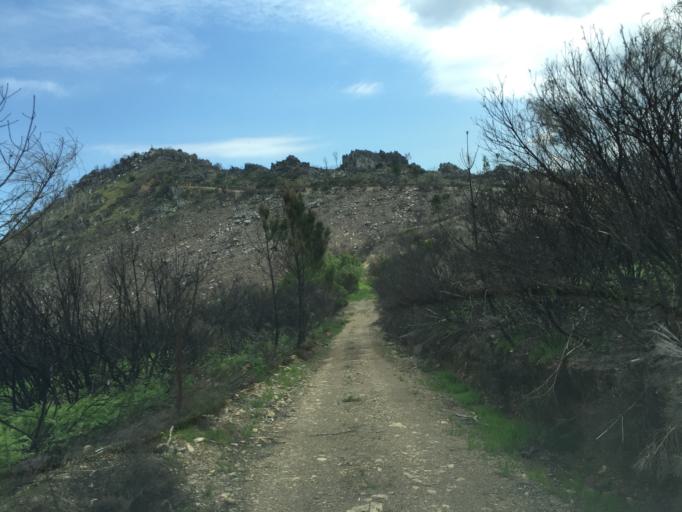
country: PT
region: Coimbra
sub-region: Pampilhosa da Serra
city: Pampilhosa da Serra
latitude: 40.1584
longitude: -7.9304
